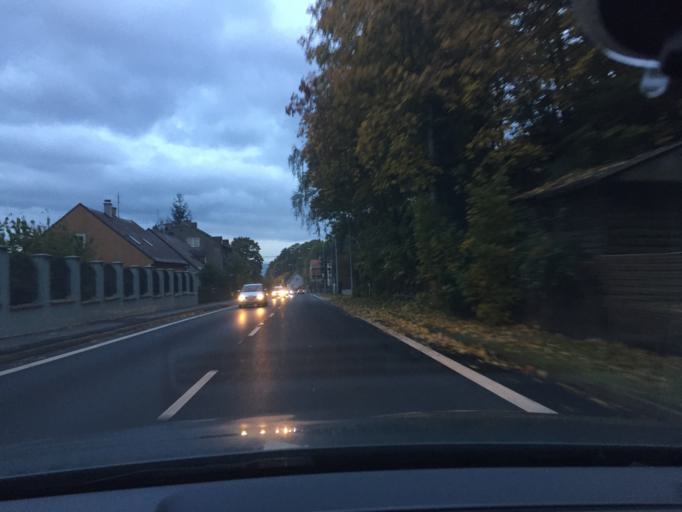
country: CZ
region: Ustecky
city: Dubi
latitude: 50.6809
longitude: 13.7888
